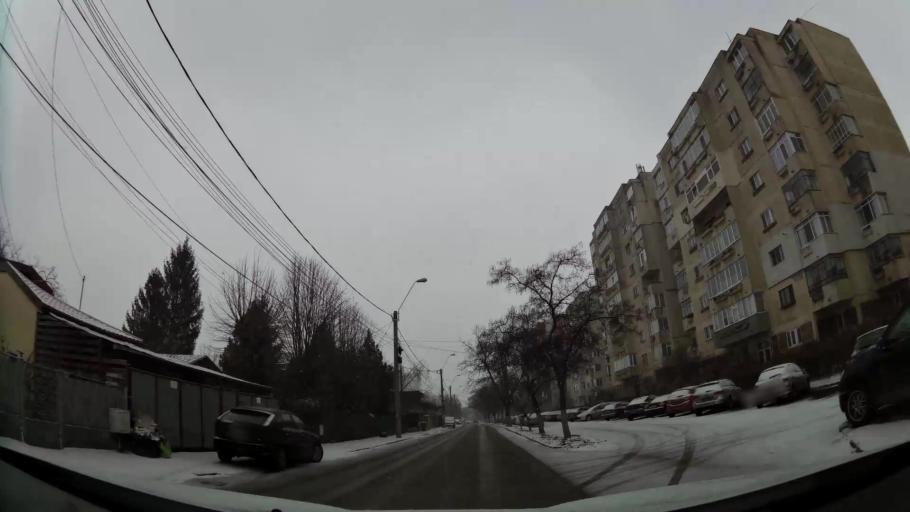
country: RO
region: Prahova
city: Ploiesti
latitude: 44.9317
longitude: 26.0072
